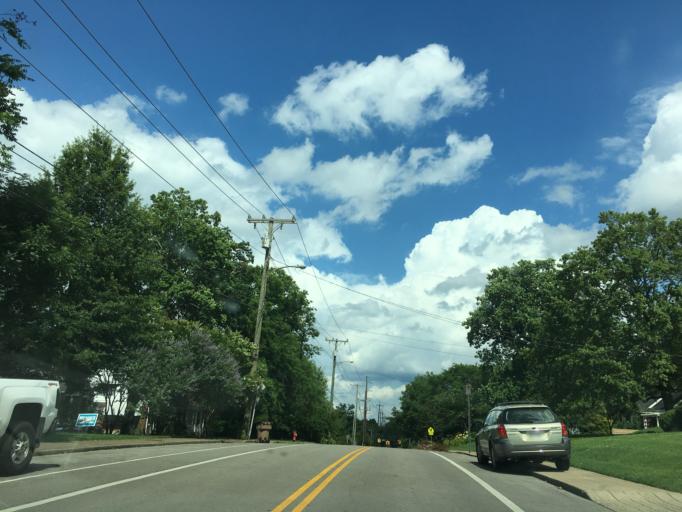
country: US
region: Tennessee
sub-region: Davidson County
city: Nashville
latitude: 36.1353
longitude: -86.8136
